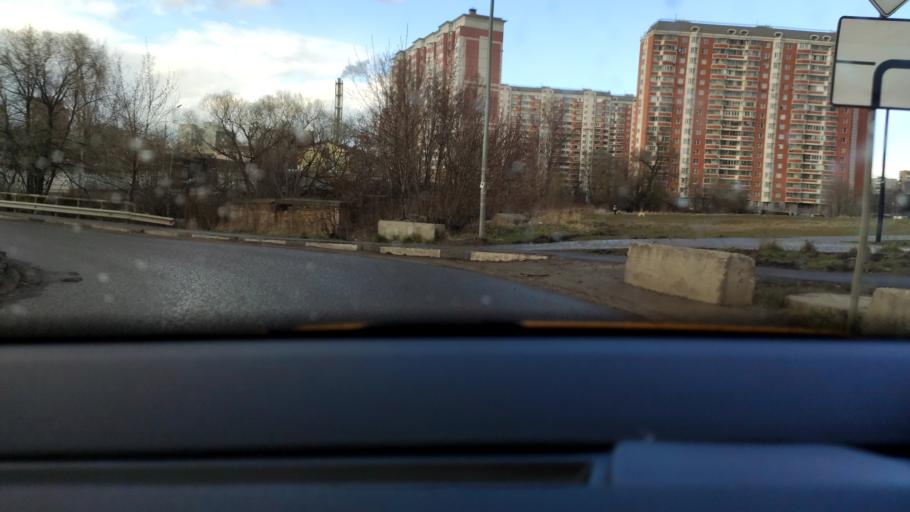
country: RU
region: Moskovskaya
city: Saltykovka
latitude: 55.7431
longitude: 37.9591
